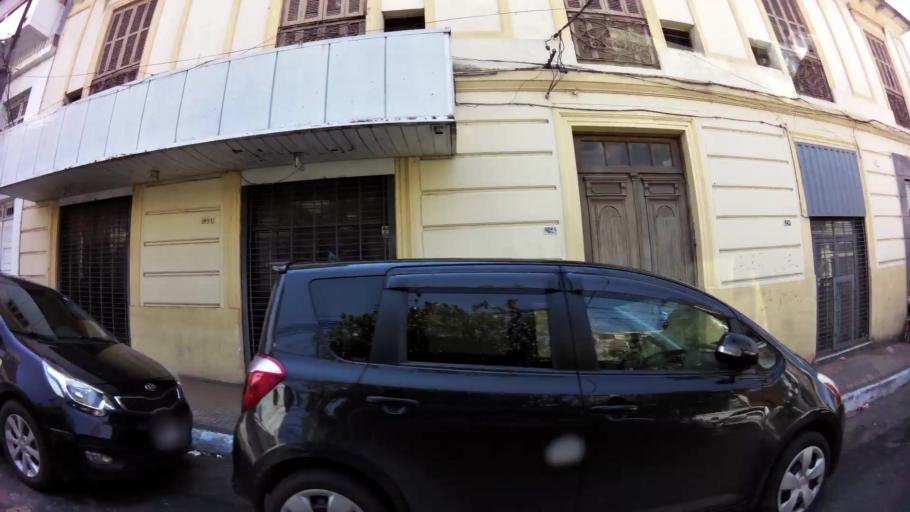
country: PY
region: Asuncion
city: Asuncion
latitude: -25.2809
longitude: -57.6364
